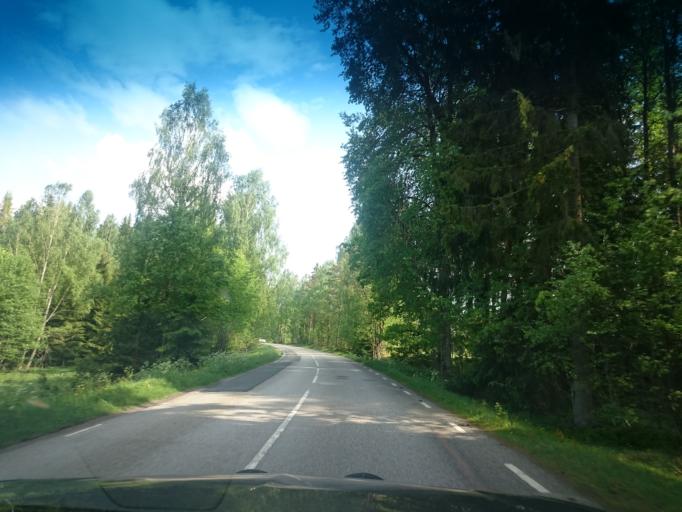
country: SE
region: Joenkoeping
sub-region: Vetlanda Kommun
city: Vetlanda
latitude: 57.3648
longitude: 15.0600
